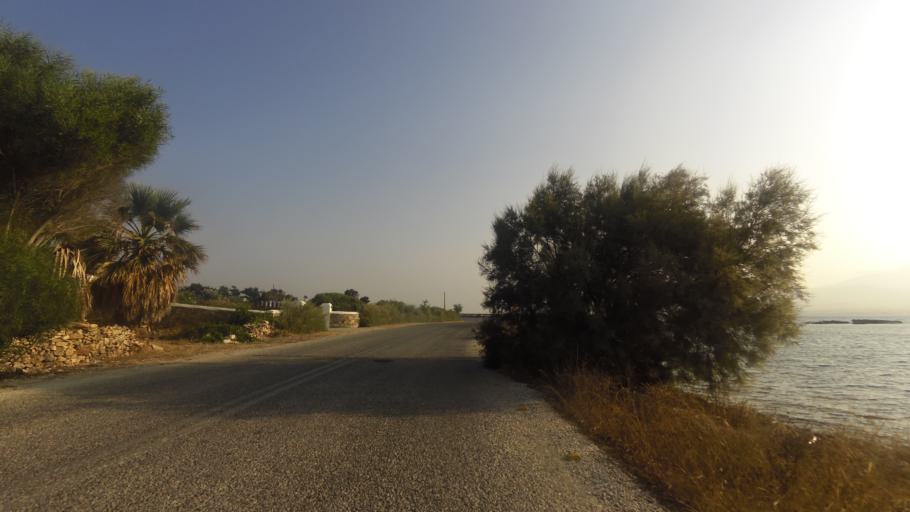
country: GR
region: South Aegean
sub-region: Nomos Kykladon
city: Antiparos
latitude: 37.0116
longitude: 25.0751
